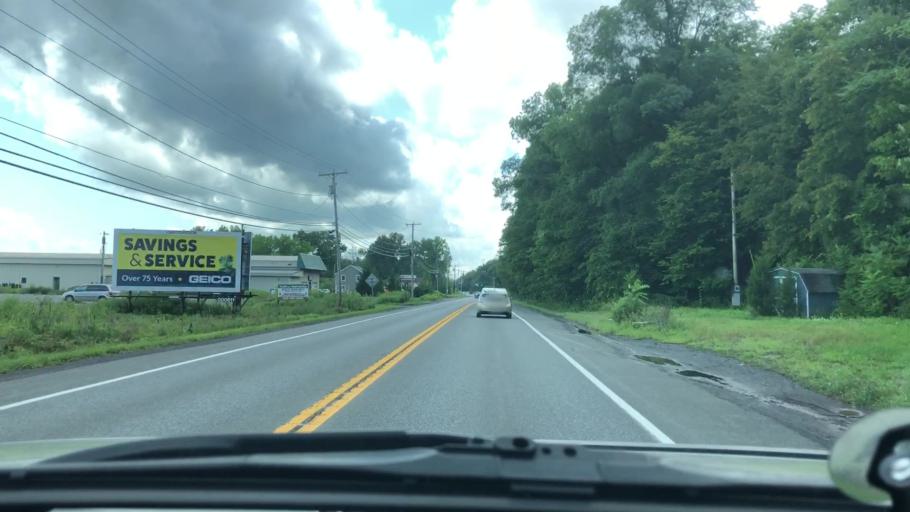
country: US
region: New York
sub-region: Ulster County
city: Saugerties
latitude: 42.0990
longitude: -73.9708
